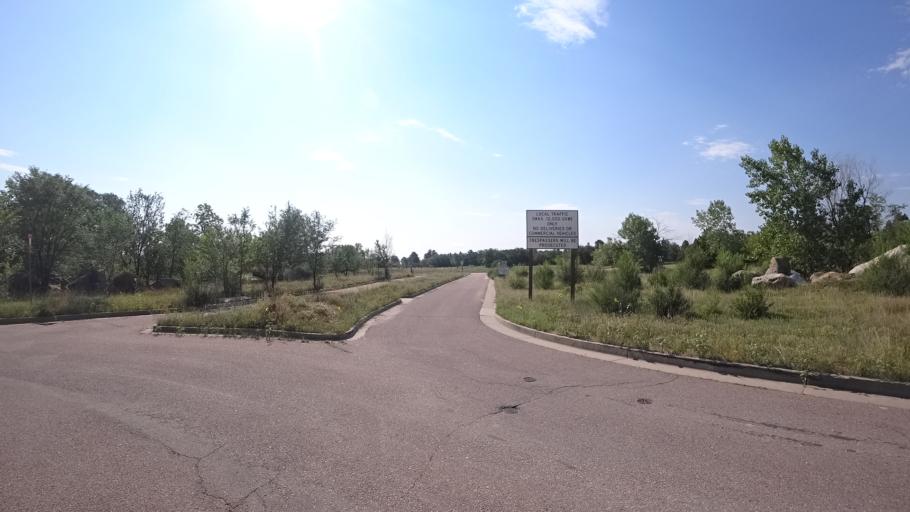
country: US
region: Colorado
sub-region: El Paso County
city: Fort Carson
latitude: 38.7478
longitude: -104.8272
